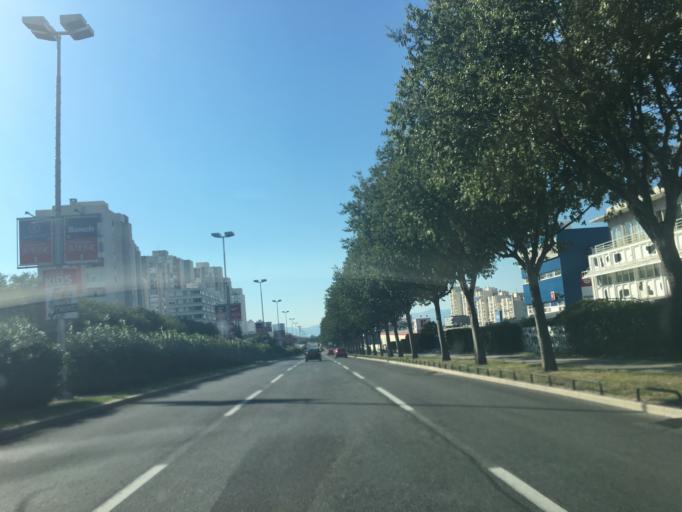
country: HR
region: Splitsko-Dalmatinska
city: Vranjic
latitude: 43.5195
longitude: 16.4699
